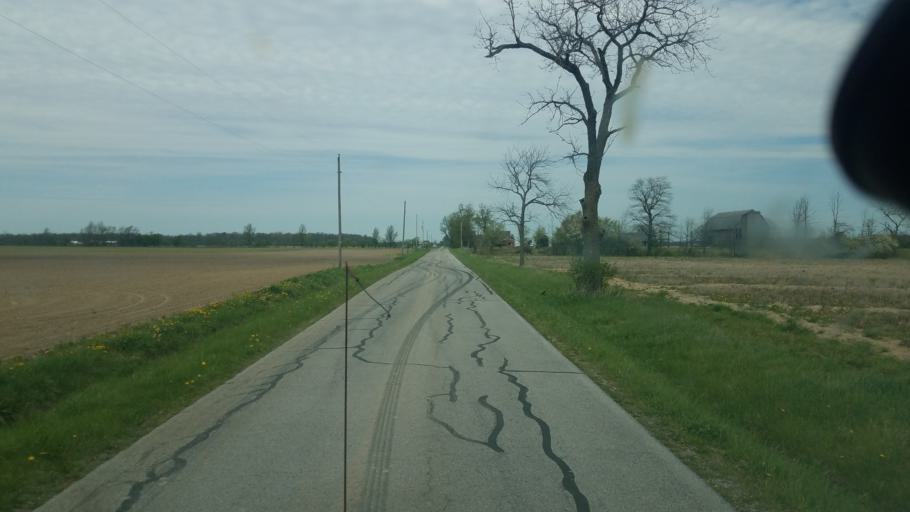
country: US
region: Ohio
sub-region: Hardin County
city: Ada
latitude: 40.8398
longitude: -83.7469
